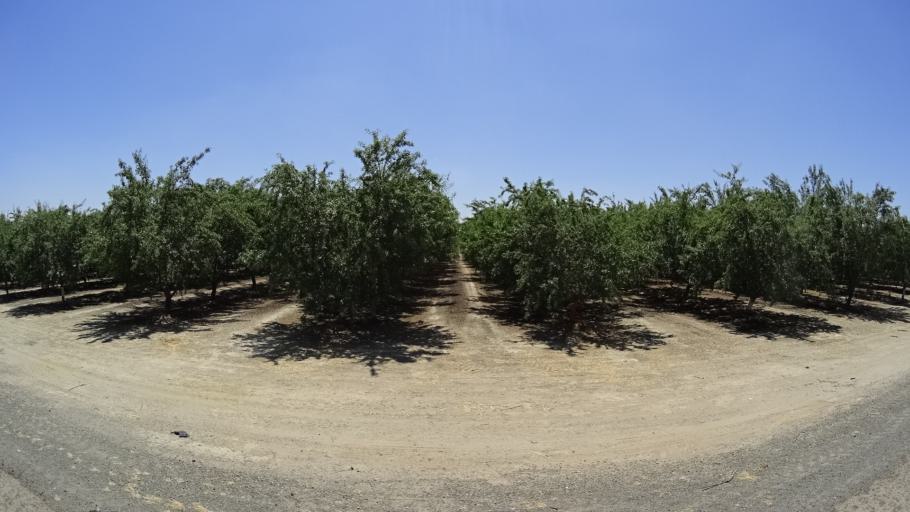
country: US
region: California
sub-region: Fresno County
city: Kingsburg
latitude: 36.4306
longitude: -119.5407
